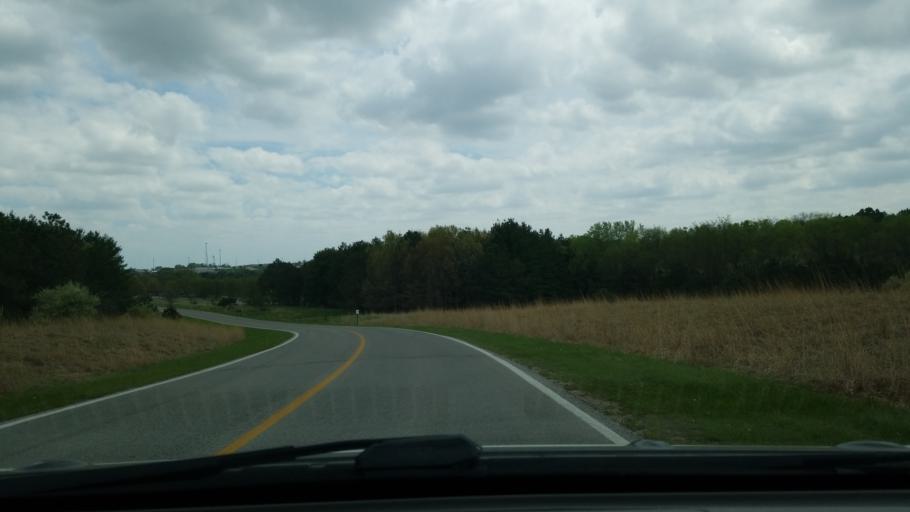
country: US
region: Nebraska
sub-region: Sarpy County
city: Chalco
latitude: 41.1649
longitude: -96.1633
